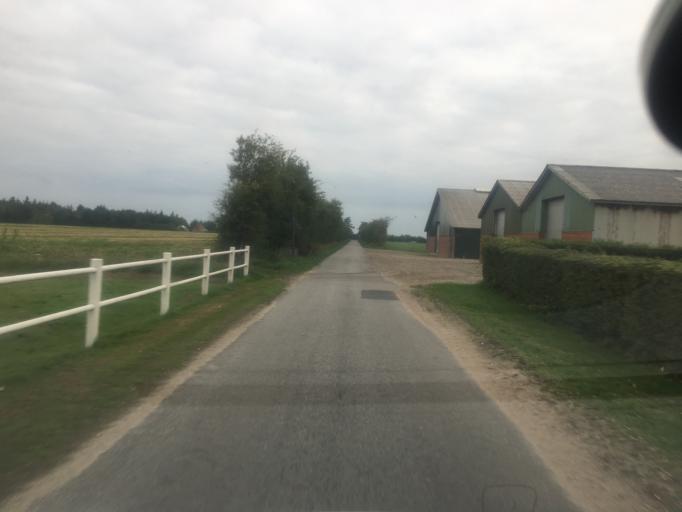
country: DK
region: South Denmark
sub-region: Tonder Kommune
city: Logumkloster
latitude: 55.0381
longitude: 9.0088
